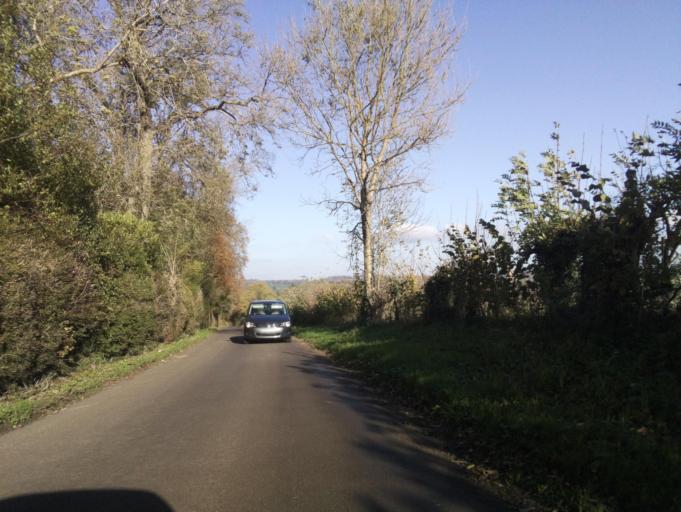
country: GB
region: England
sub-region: Somerset
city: Castle Cary
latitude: 51.0308
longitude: -2.4990
